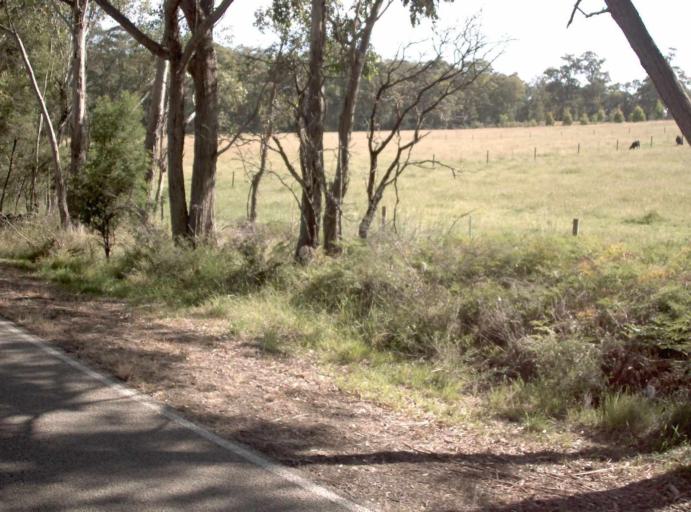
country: AU
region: Victoria
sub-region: East Gippsland
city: Lakes Entrance
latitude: -37.7488
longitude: 147.8141
